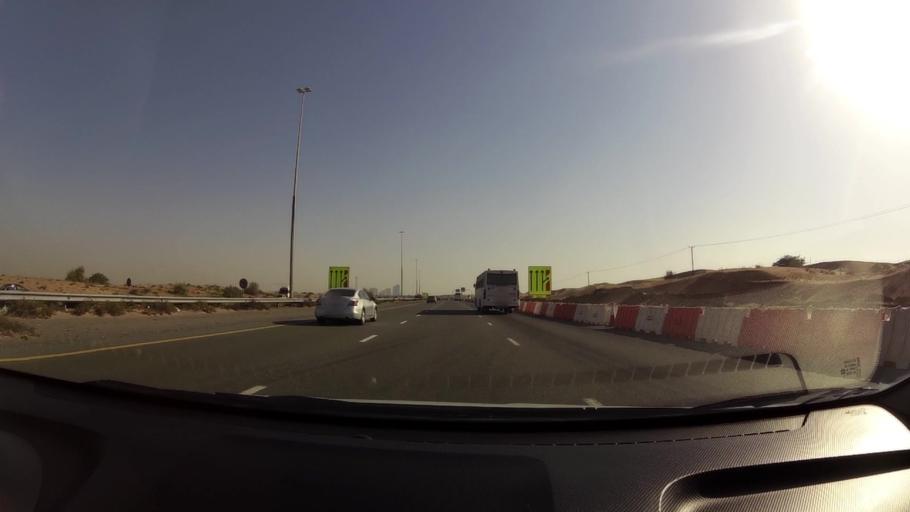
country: AE
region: Umm al Qaywayn
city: Umm al Qaywayn
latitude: 25.4361
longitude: 55.5989
